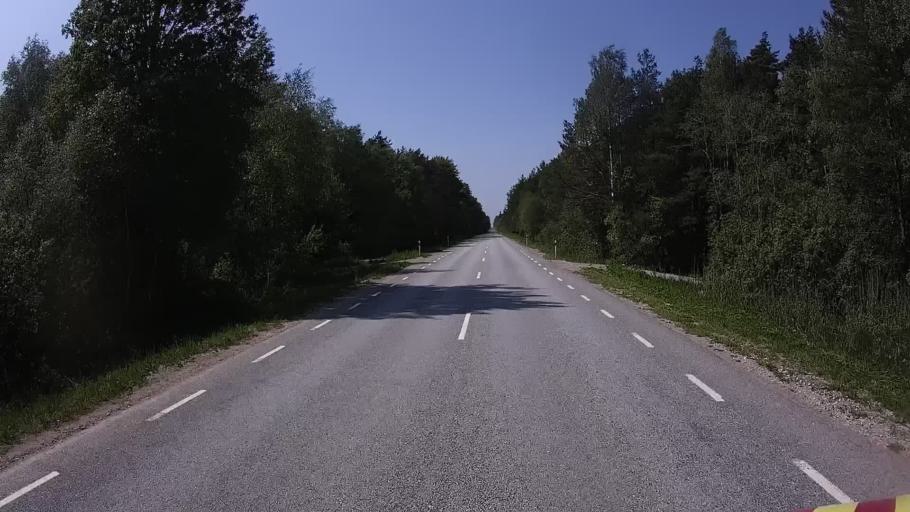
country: EE
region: Saare
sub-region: Kuressaare linn
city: Kuressaare
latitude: 58.3398
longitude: 22.1734
